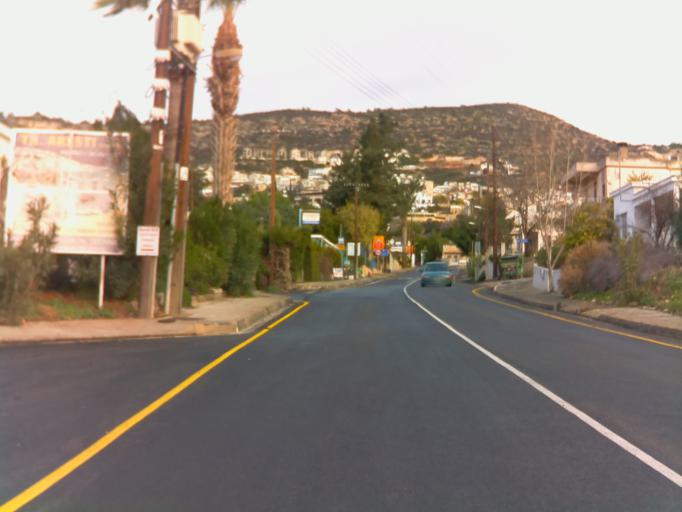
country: CY
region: Pafos
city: Pegeia
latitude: 34.8797
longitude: 32.3801
